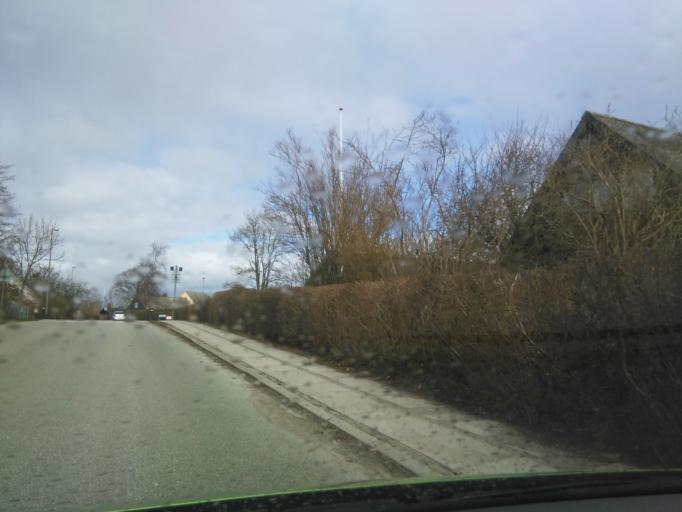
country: DK
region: Central Jutland
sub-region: Arhus Kommune
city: Marslet
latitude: 56.0697
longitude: 10.1568
